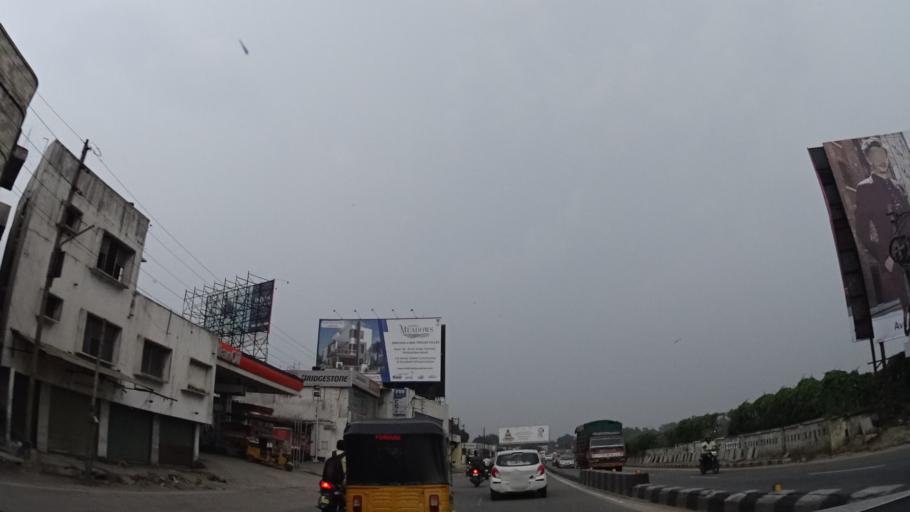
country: IN
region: Telangana
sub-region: Hyderabad
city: Malkajgiri
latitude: 17.4553
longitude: 78.4852
